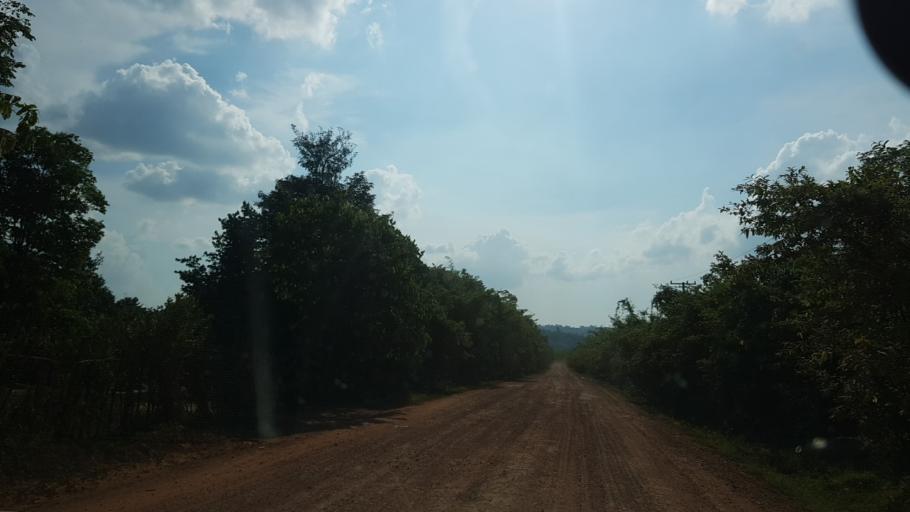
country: LA
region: Vientiane
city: Muang Phon-Hong
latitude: 18.3435
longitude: 102.2950
